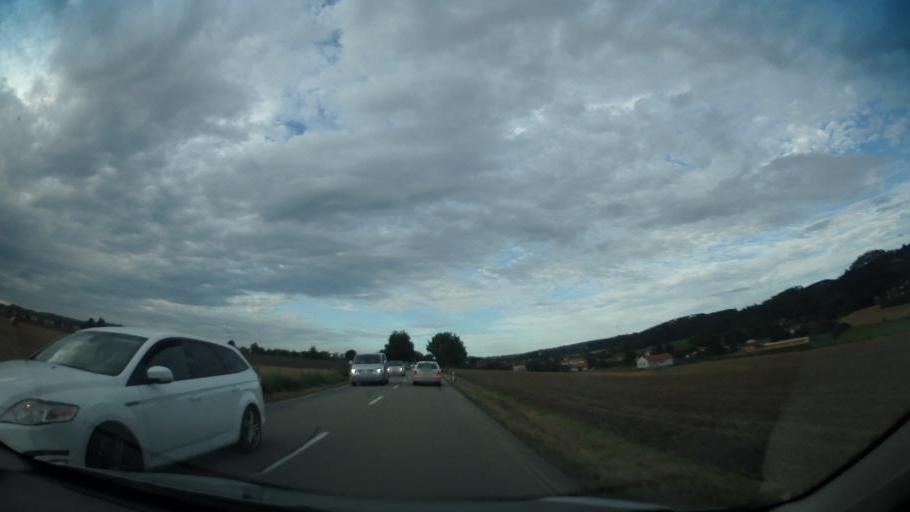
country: CZ
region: South Moravian
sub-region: Okres Blansko
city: Boskovice
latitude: 49.5270
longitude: 16.6844
